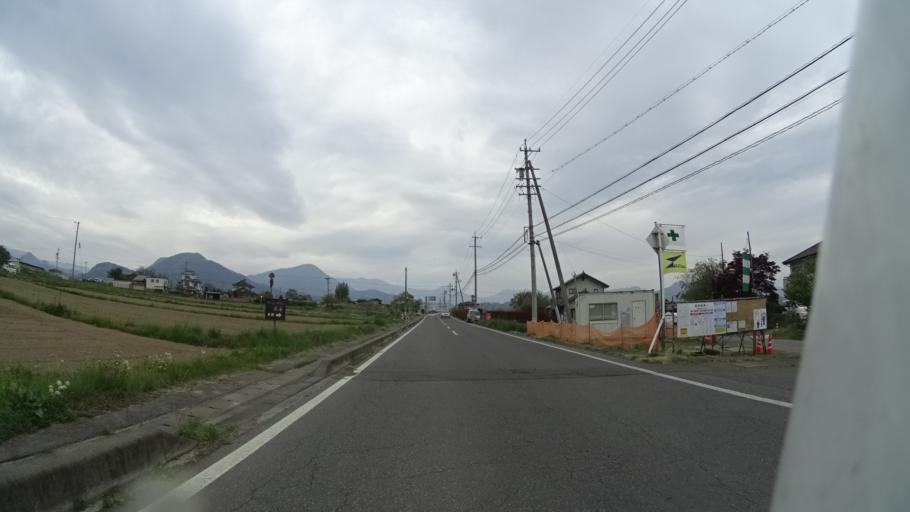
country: JP
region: Nagano
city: Kamimaruko
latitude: 36.3492
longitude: 138.1993
